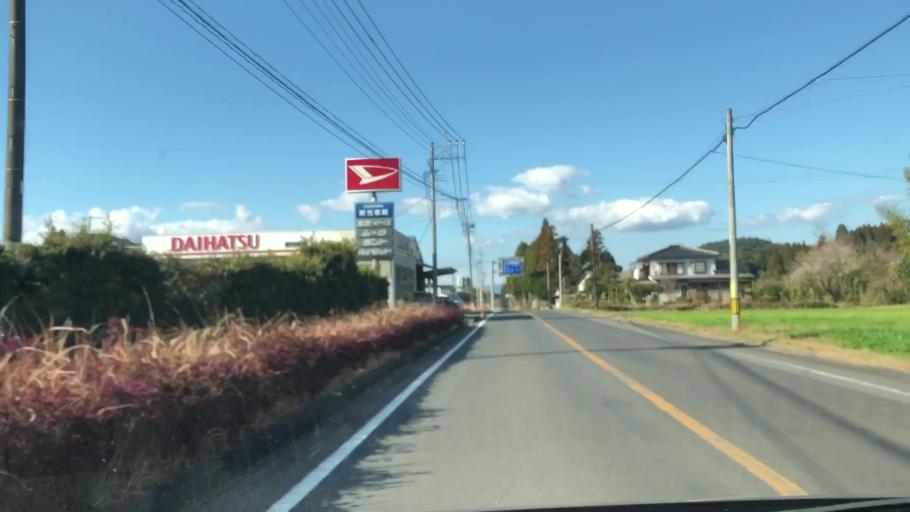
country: JP
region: Kagoshima
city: Satsumasendai
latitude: 31.7977
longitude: 130.4404
